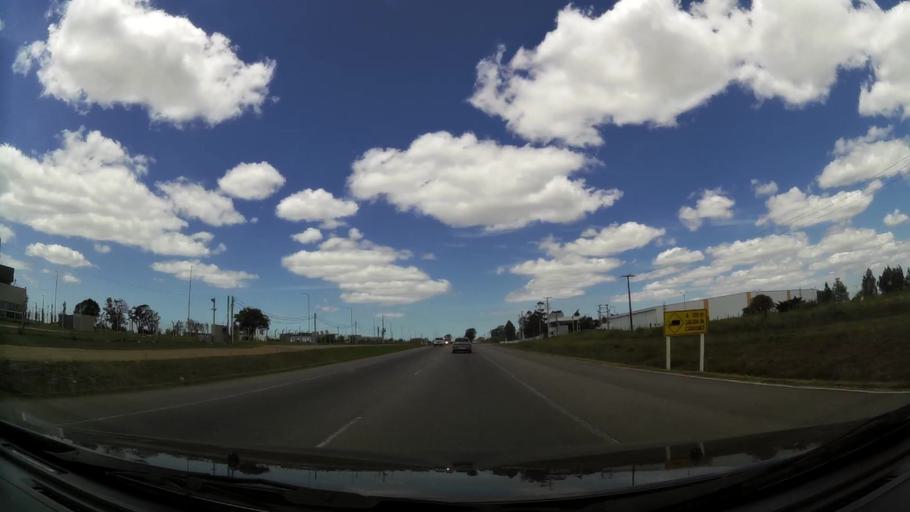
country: UY
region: Canelones
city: Colonia Nicolich
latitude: -34.8094
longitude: -56.0062
